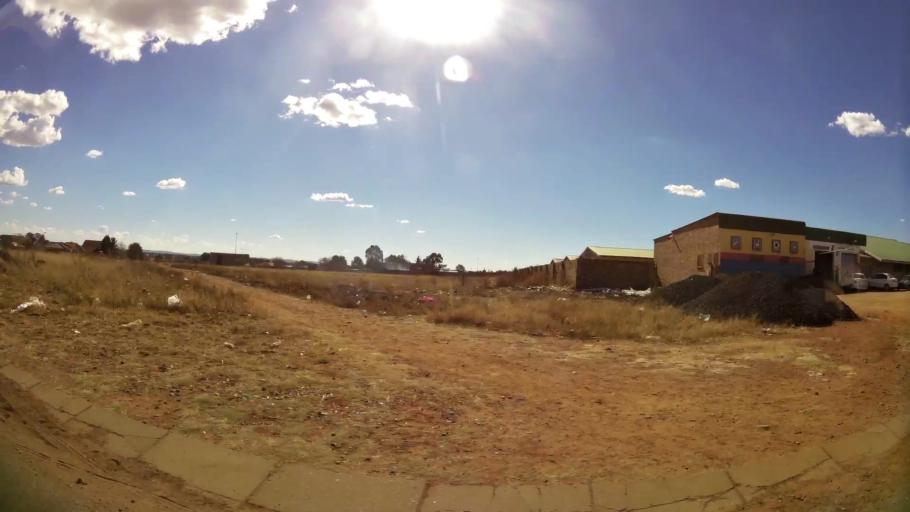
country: ZA
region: North-West
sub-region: Dr Kenneth Kaunda District Municipality
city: Klerksdorp
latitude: -26.8755
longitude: 26.5890
